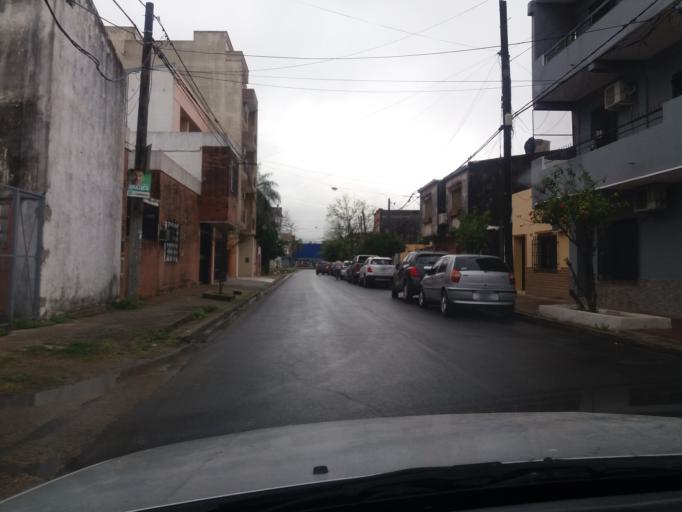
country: AR
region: Corrientes
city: Corrientes
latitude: -27.4767
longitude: -58.8432
